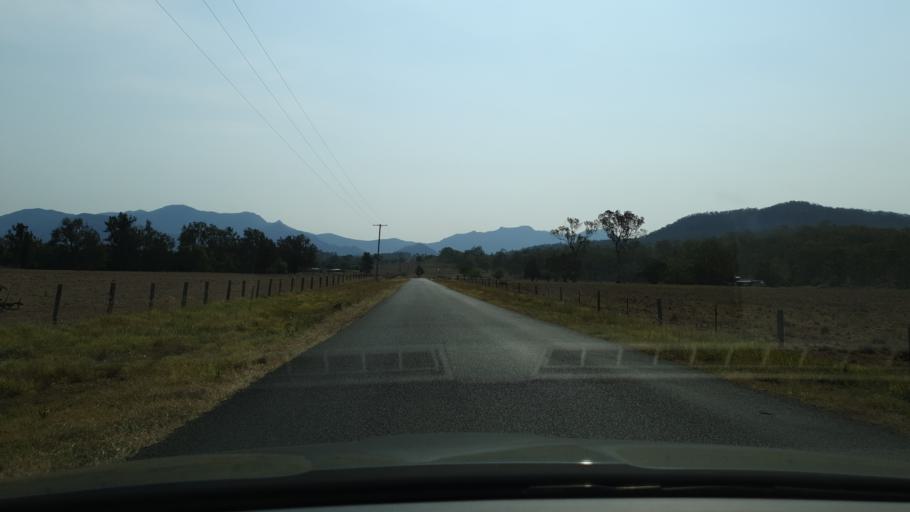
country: AU
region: Queensland
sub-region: Ipswich
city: Deebing Heights
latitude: -28.1381
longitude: 152.5767
